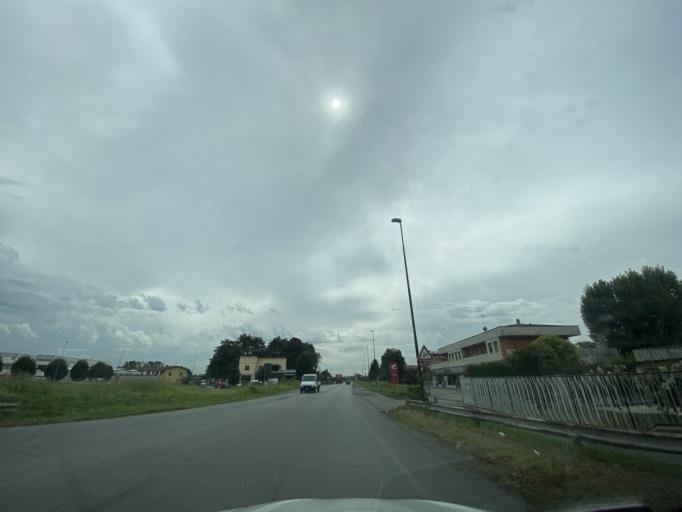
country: IT
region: Lombardy
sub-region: Citta metropolitana di Milano
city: Pessano Con Bornago
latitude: 45.5421
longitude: 9.3920
